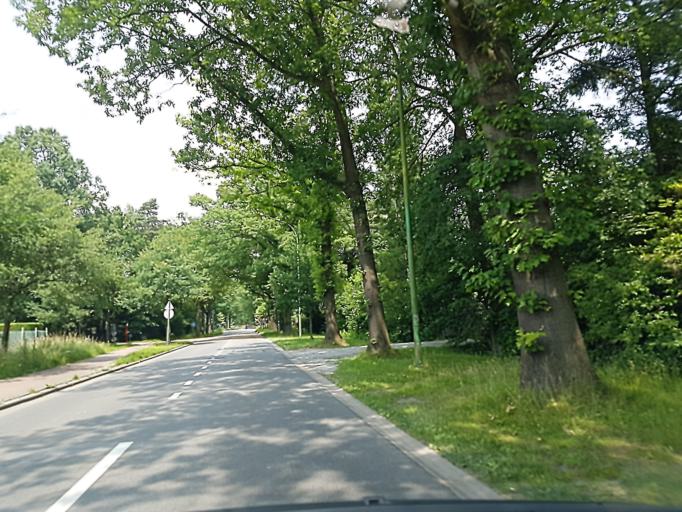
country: BE
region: Flanders
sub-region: Provincie Antwerpen
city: Wijnegem
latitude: 51.2411
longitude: 4.5387
